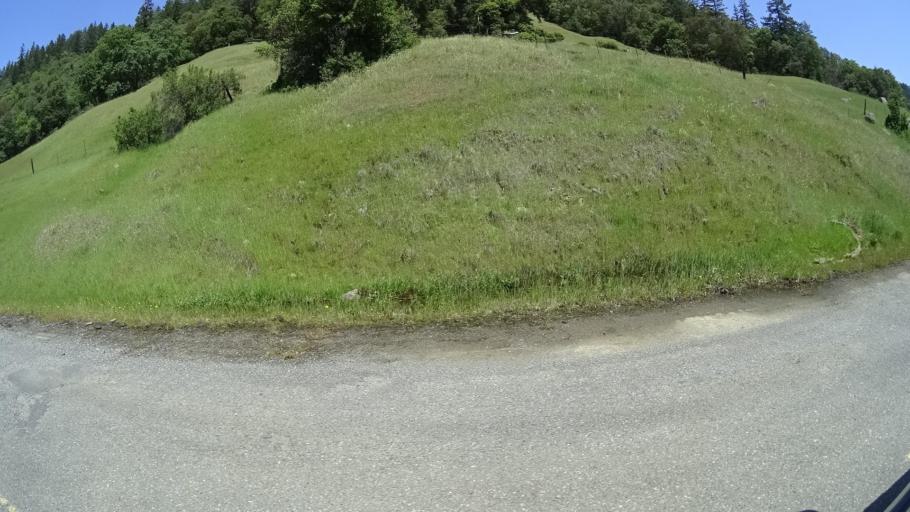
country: US
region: California
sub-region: Humboldt County
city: Redway
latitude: 40.2255
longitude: -123.6405
